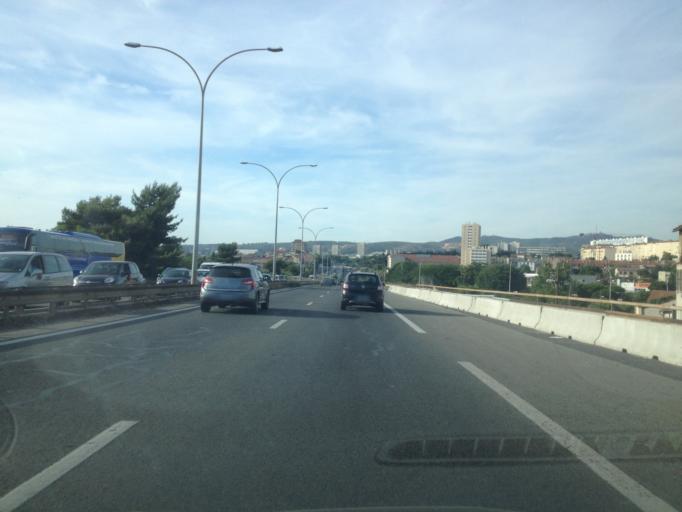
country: FR
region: Provence-Alpes-Cote d'Azur
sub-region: Departement des Bouches-du-Rhone
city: Marseille 03
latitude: 43.3167
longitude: 5.3772
